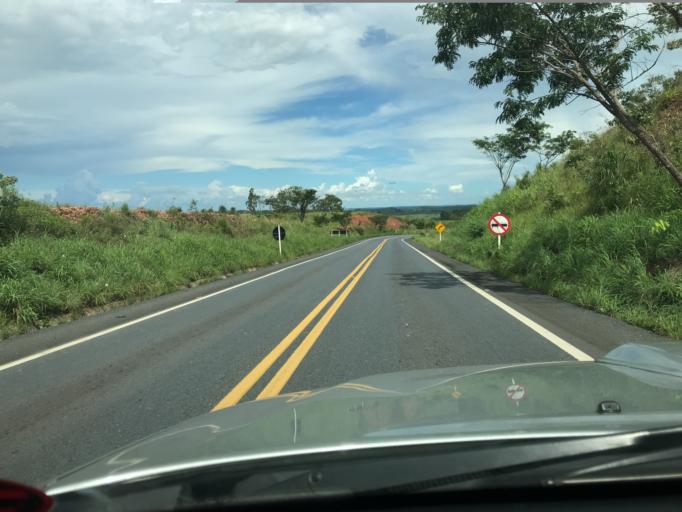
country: BR
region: Minas Gerais
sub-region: Campos Altos
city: Campos Altos
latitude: -19.7951
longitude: -46.0363
